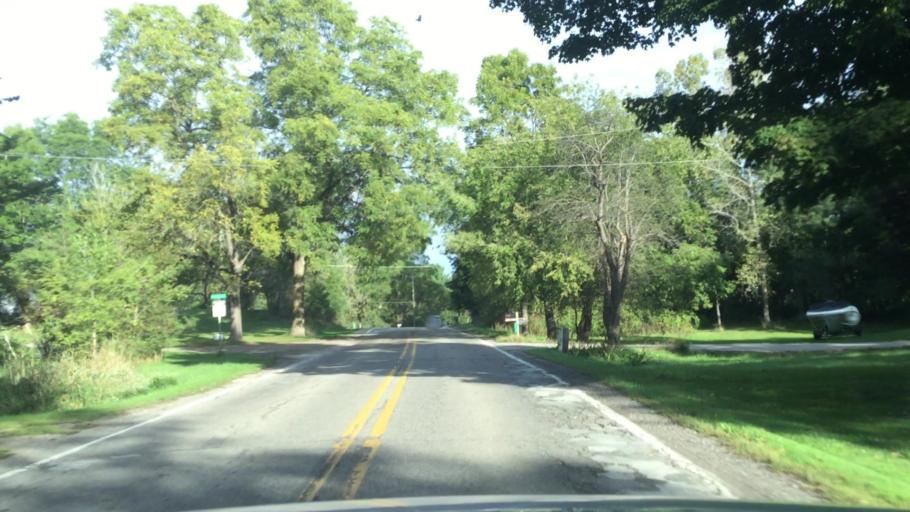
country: US
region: Michigan
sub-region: Livingston County
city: Brighton
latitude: 42.4837
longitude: -83.8502
